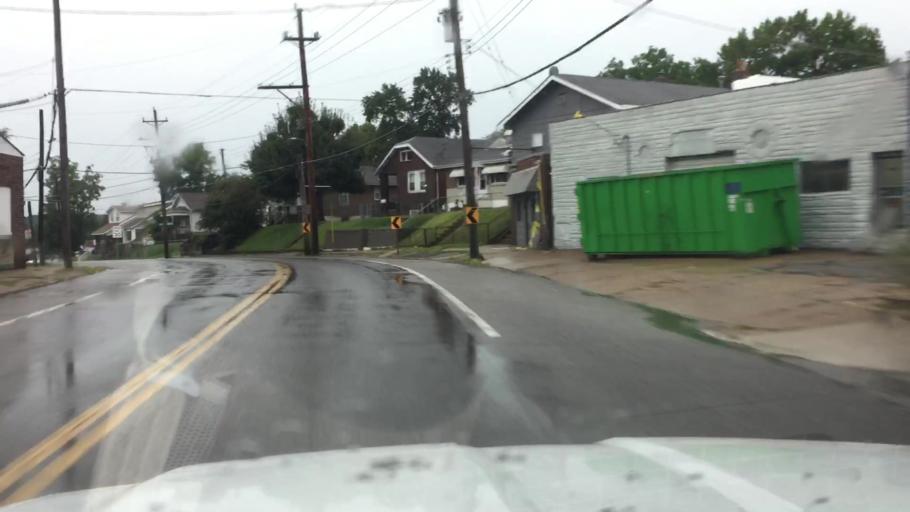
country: US
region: Missouri
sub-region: Saint Louis County
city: Lemay
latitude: 38.5323
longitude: -90.2769
